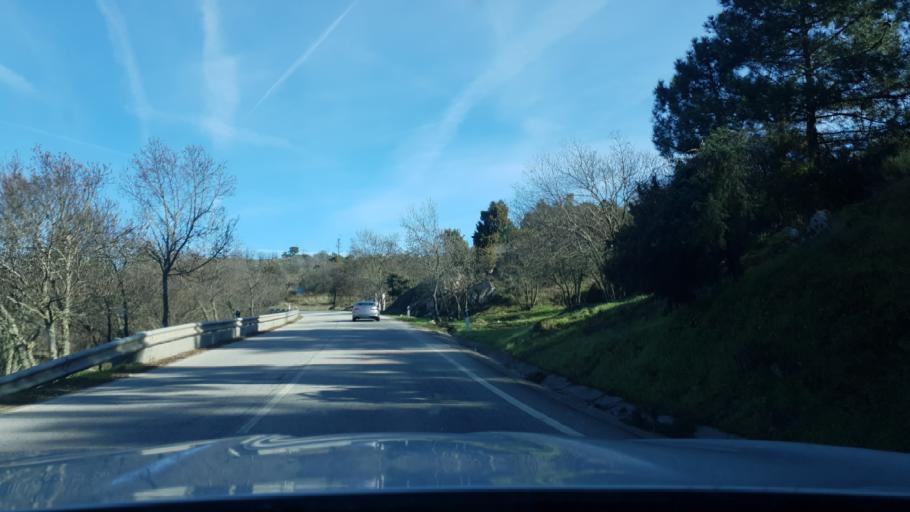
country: PT
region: Braganca
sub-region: Torre de Moncorvo
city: Torre de Moncorvo
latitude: 41.1818
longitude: -7.0246
